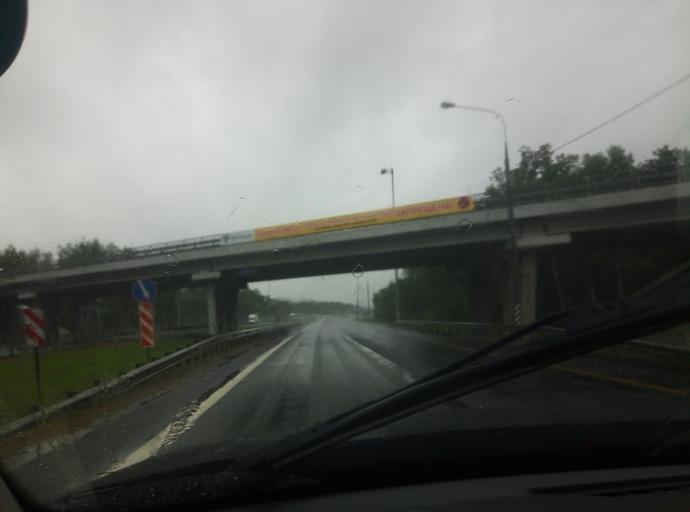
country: RU
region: Moskovskaya
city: Danki
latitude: 54.9171
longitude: 37.5138
